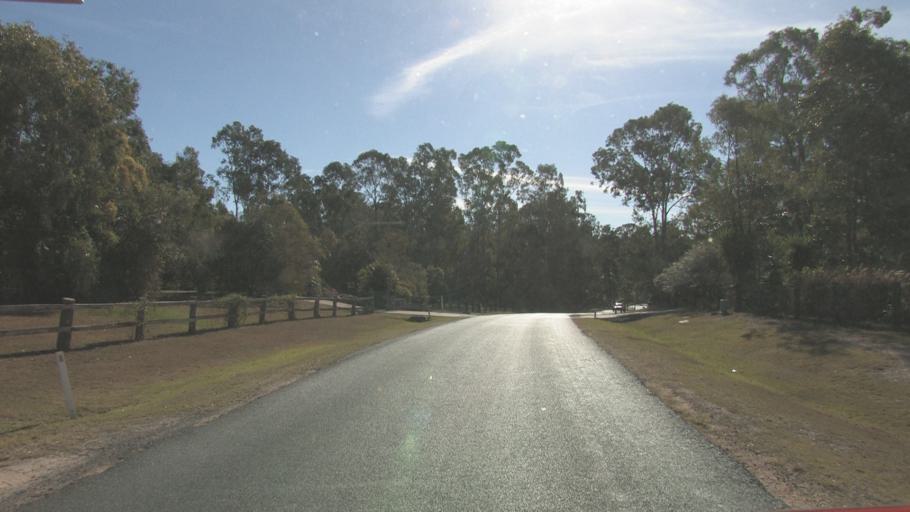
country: AU
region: Queensland
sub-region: Ipswich
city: Springfield Lakes
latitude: -27.7300
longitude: 152.9235
